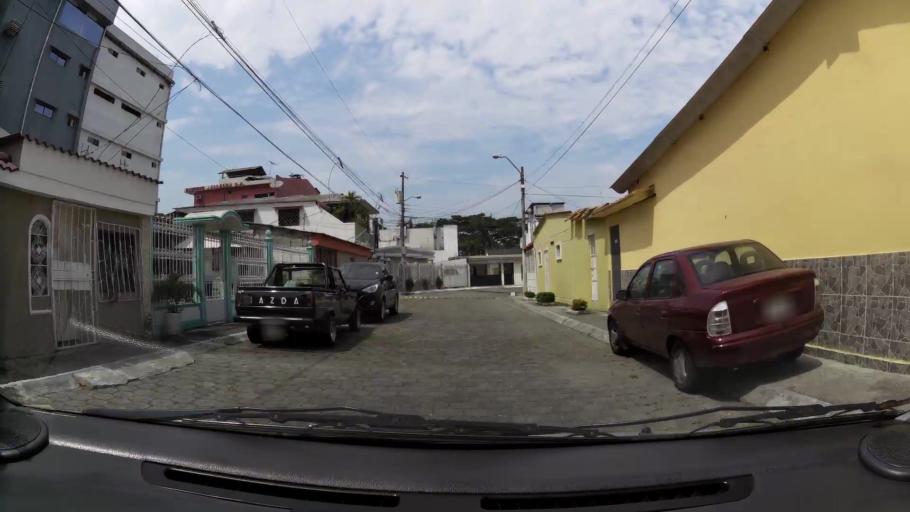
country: EC
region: Guayas
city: Eloy Alfaro
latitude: -2.1339
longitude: -79.9041
